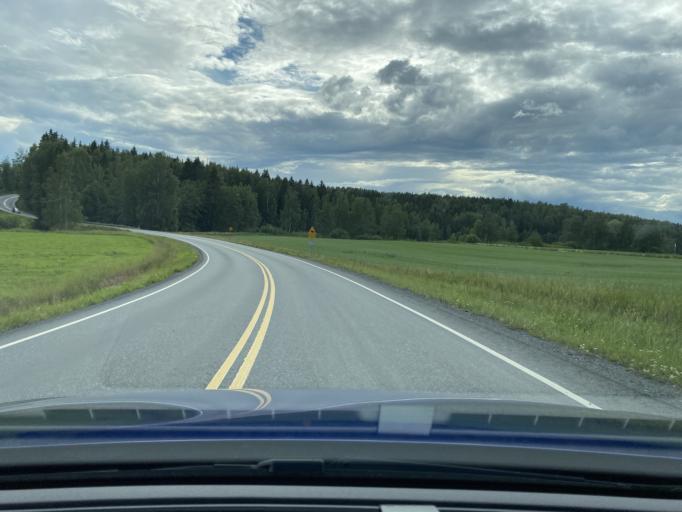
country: FI
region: Pirkanmaa
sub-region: Tampere
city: Vesilahti
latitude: 61.2898
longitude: 23.5998
